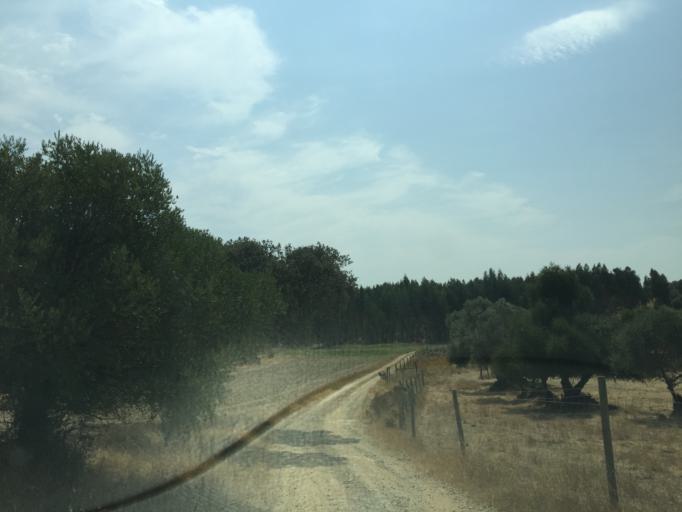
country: PT
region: Setubal
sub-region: Grandola
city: Grandola
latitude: 38.0431
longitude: -8.4774
